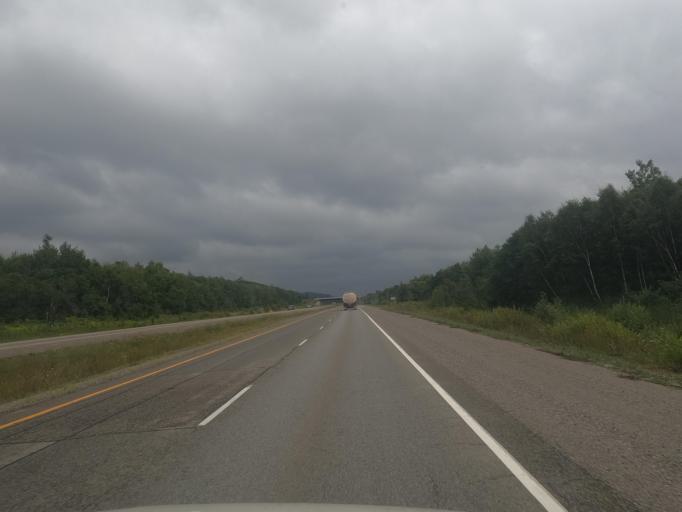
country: CA
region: Ontario
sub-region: Algoma
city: Sault Ste. Marie
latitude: 46.5524
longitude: -84.1598
